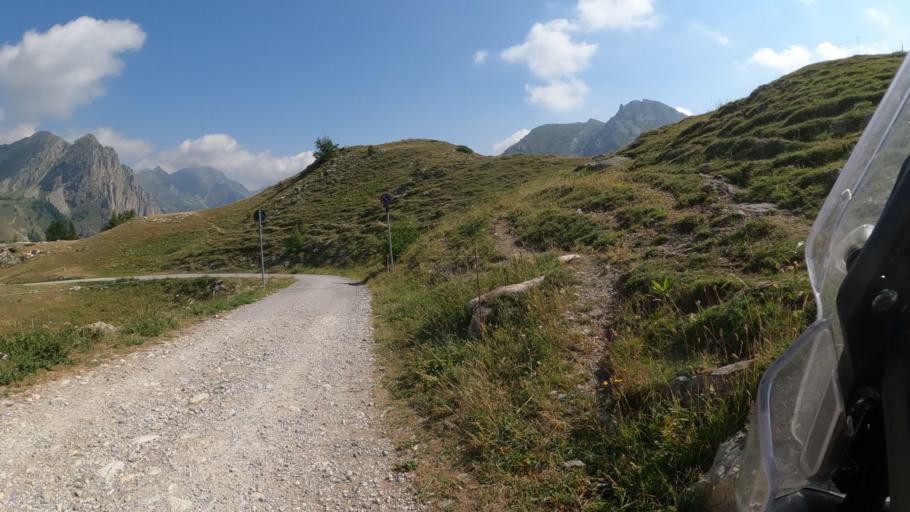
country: IT
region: Piedmont
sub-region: Provincia di Cuneo
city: Pietraporzio
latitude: 44.4042
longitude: 7.0423
